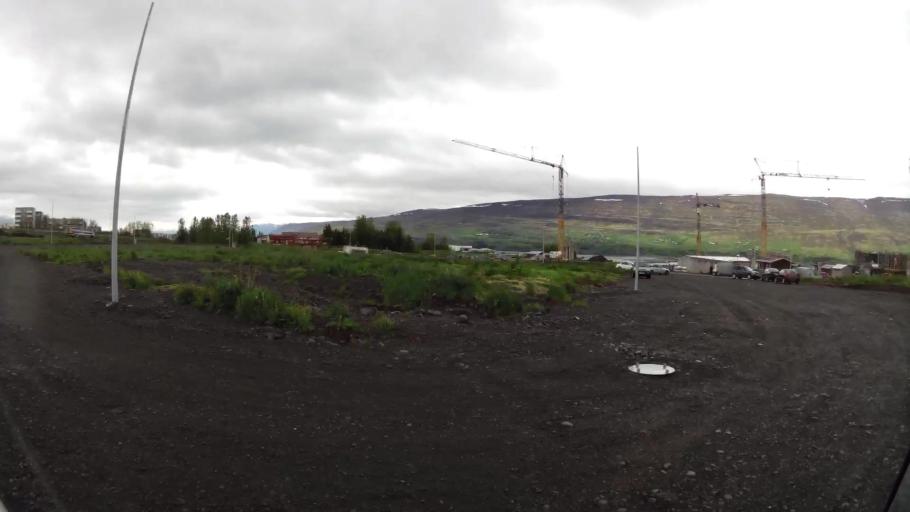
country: IS
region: Northeast
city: Akureyri
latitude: 65.6592
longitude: -18.0950
